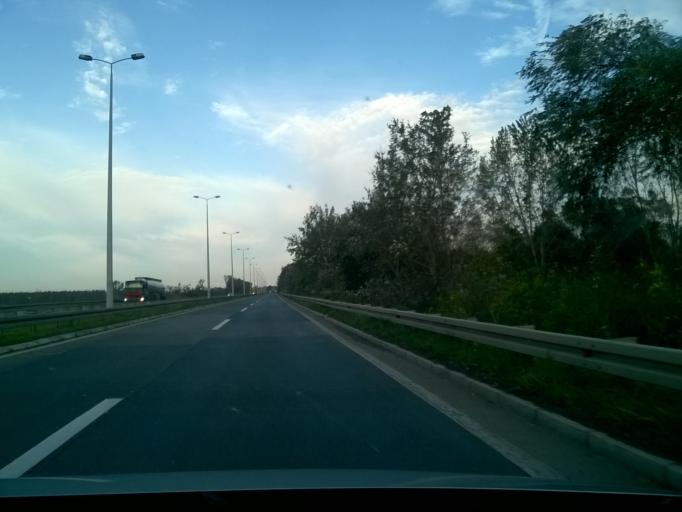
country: RS
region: Autonomna Pokrajina Vojvodina
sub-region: Juznobanatski Okrug
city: Pancevo
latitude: 44.8600
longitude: 20.5940
